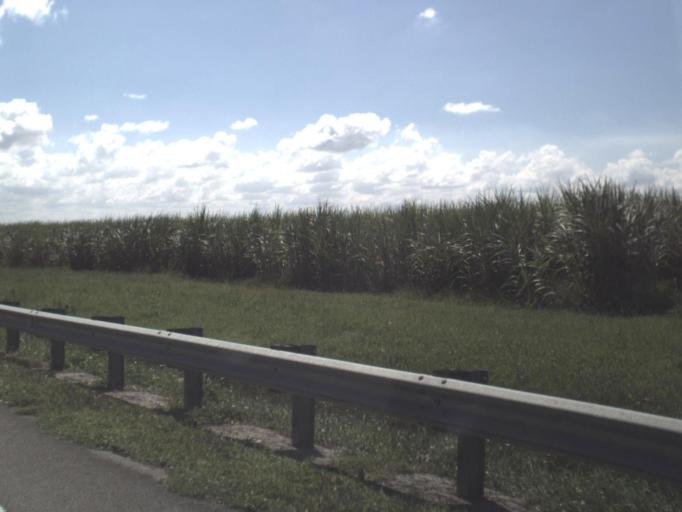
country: US
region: Florida
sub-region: Glades County
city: Moore Haven
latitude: 26.8557
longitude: -81.1228
